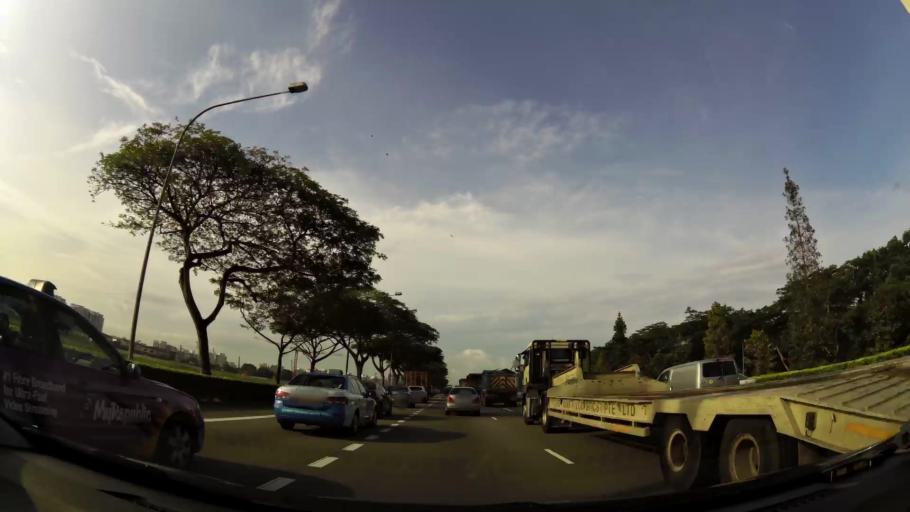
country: MY
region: Johor
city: Johor Bahru
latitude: 1.3589
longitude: 103.7016
